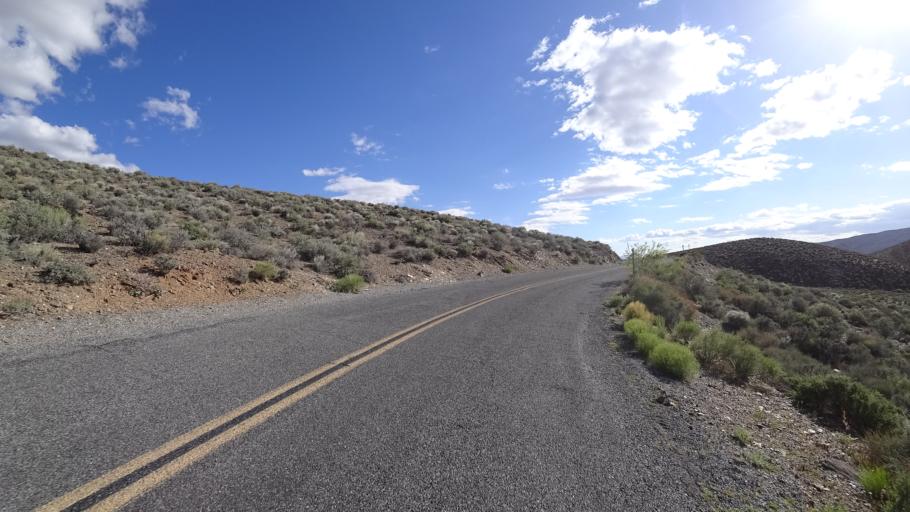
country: US
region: California
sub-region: San Bernardino County
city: Searles Valley
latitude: 36.3214
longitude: -117.1515
